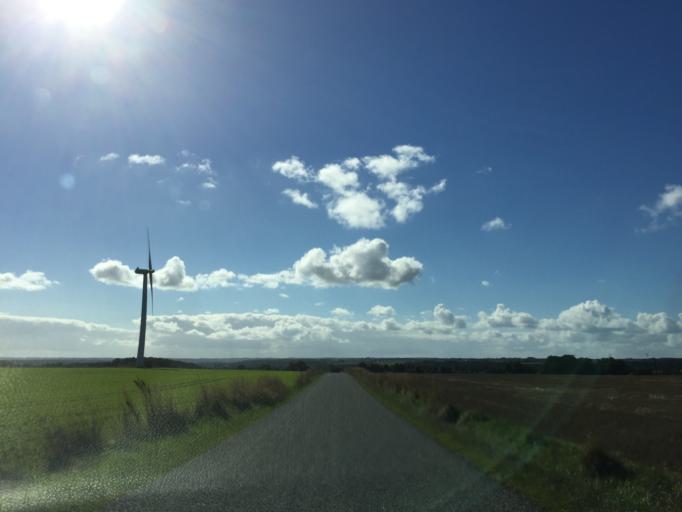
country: DK
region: Central Jutland
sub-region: Viborg Kommune
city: Bjerringbro
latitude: 56.2578
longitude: 9.6884
